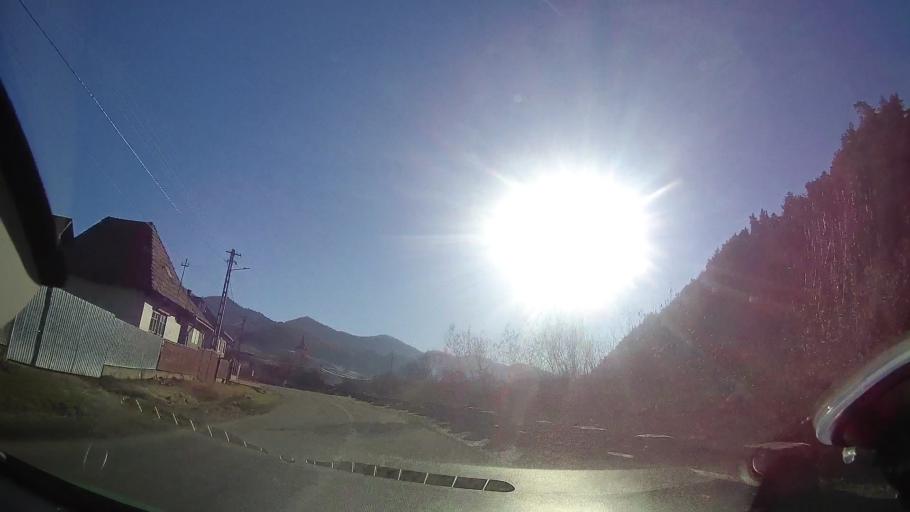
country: RO
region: Cluj
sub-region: Comuna Sacueu
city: Sacuieu
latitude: 46.8242
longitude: 22.8853
